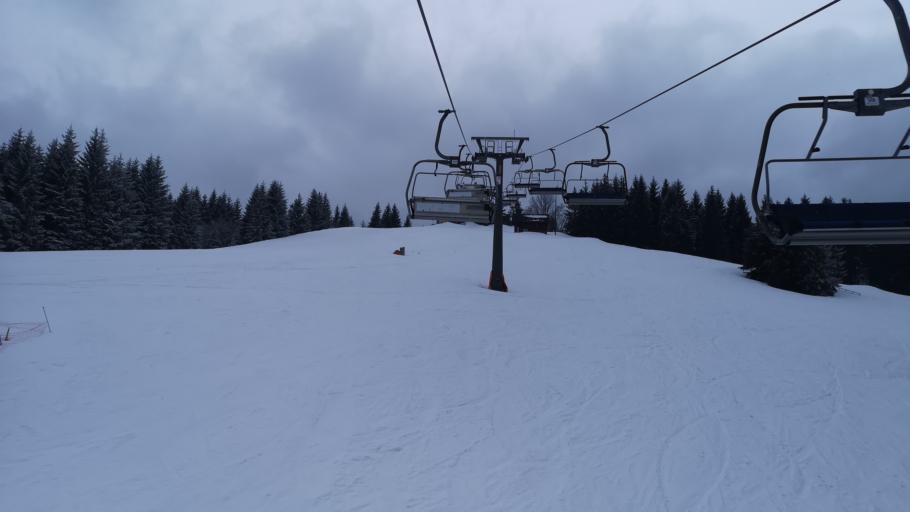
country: SK
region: Zilinsky
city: Ruzomberok
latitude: 49.0498
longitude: 19.2512
